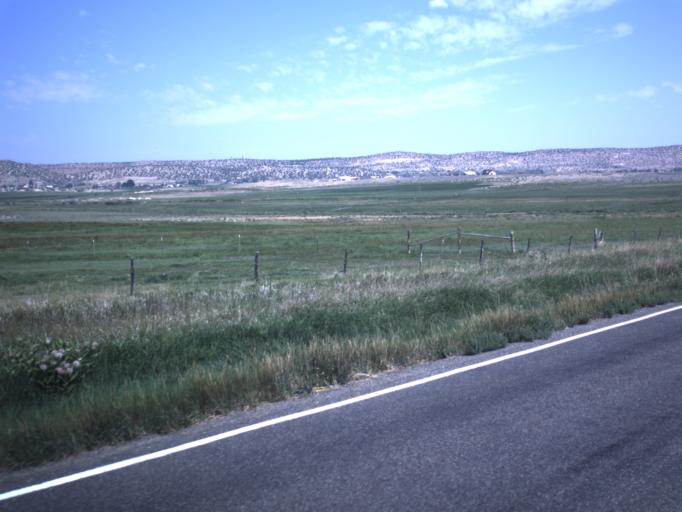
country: US
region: Utah
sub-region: Daggett County
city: Manila
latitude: 40.9613
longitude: -109.7130
